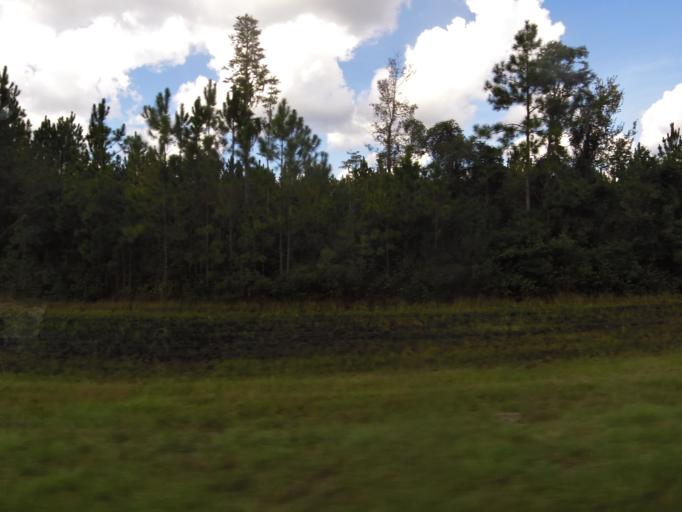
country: US
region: Florida
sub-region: Hamilton County
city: Jasper
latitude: 30.6714
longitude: -82.7594
